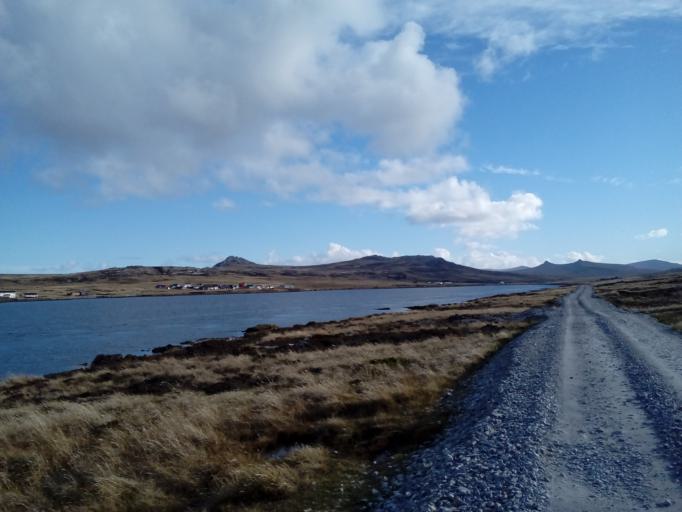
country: FK
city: Stanley
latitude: -51.6843
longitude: -57.8949
